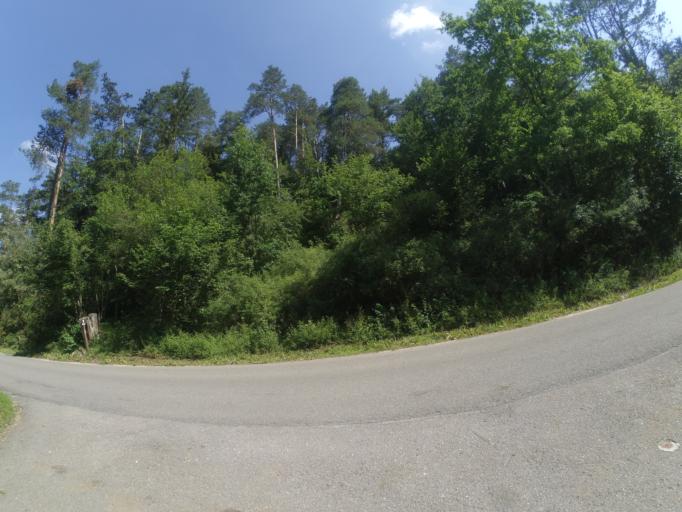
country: DE
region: Baden-Wuerttemberg
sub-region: Tuebingen Region
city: Dornstadt
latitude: 48.4548
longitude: 9.9036
